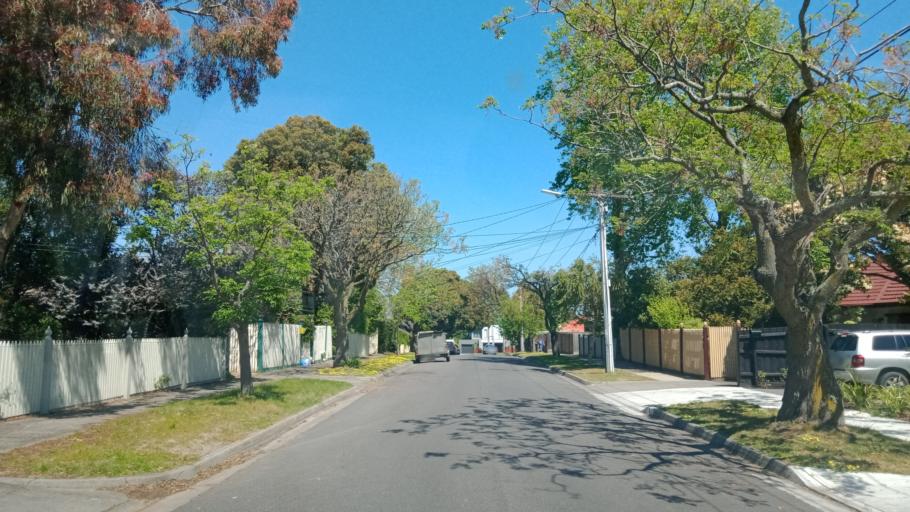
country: AU
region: Victoria
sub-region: Monash
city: Oakleigh South
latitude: -37.9250
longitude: 145.0760
